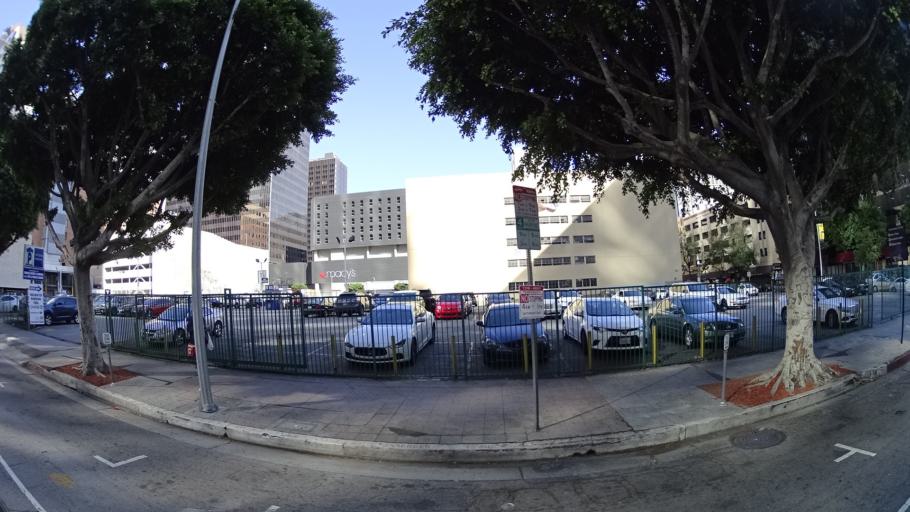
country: US
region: California
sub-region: Los Angeles County
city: Los Angeles
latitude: 34.0481
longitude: -118.2609
